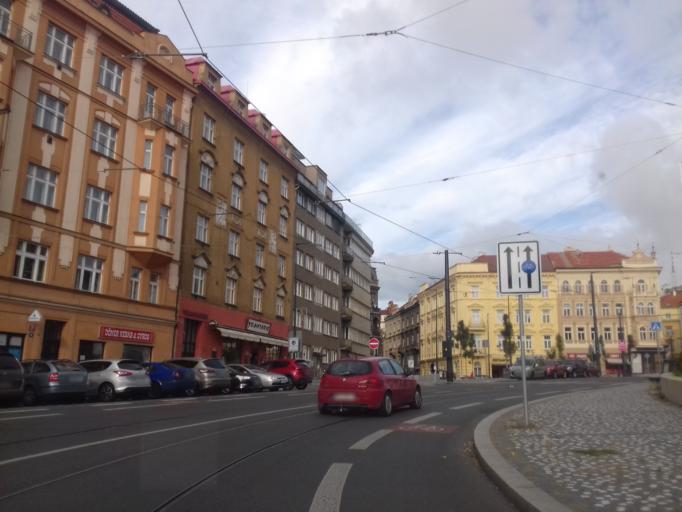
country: CZ
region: Praha
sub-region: Praha 8
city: Karlin
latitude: 50.0697
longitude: 14.4517
